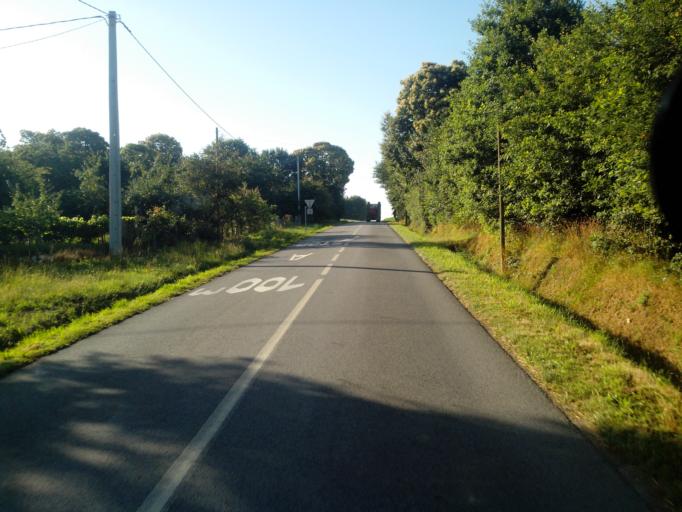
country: FR
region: Brittany
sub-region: Departement du Morbihan
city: Guilliers
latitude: 48.0804
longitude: -2.4404
